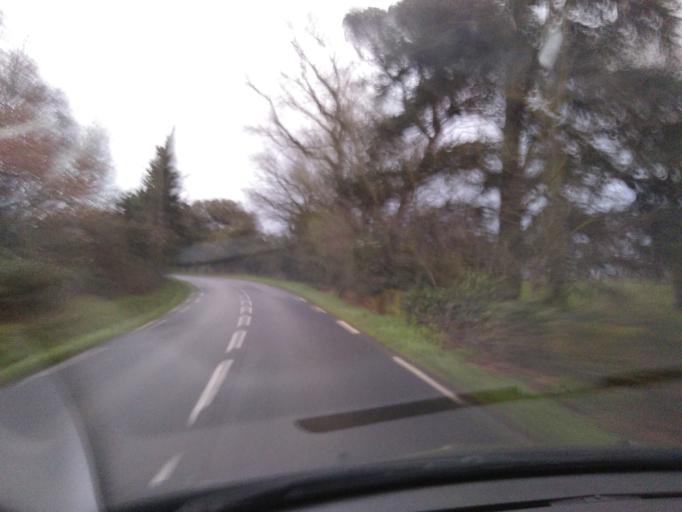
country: FR
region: Midi-Pyrenees
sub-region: Departement de la Haute-Garonne
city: Seilh
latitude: 43.6905
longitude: 1.3419
